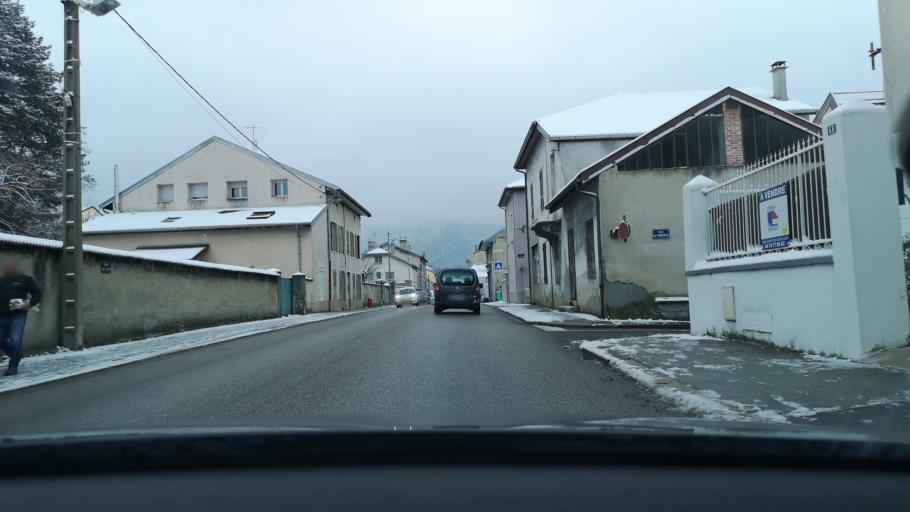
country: FR
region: Rhone-Alpes
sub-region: Departement de l'Ain
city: Oyonnax
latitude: 46.2641
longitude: 5.6596
